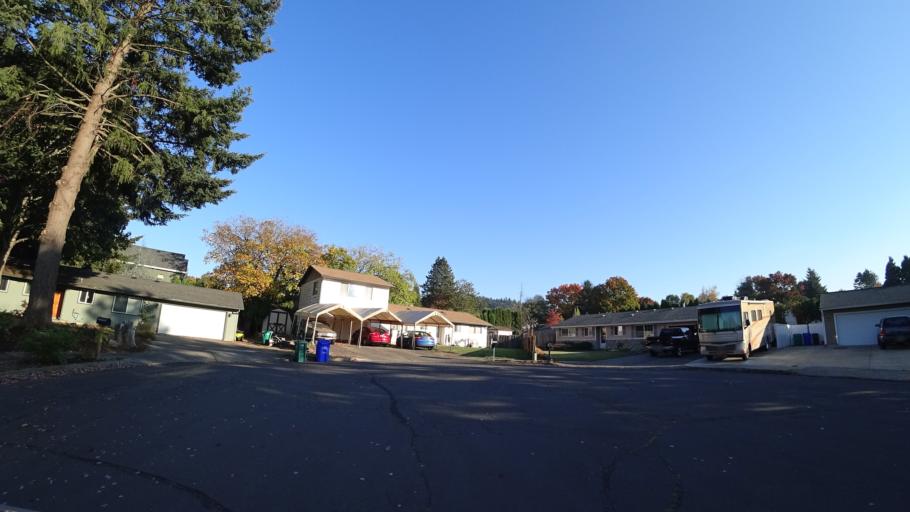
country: US
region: Oregon
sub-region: Multnomah County
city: Gresham
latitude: 45.4840
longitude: -122.4551
